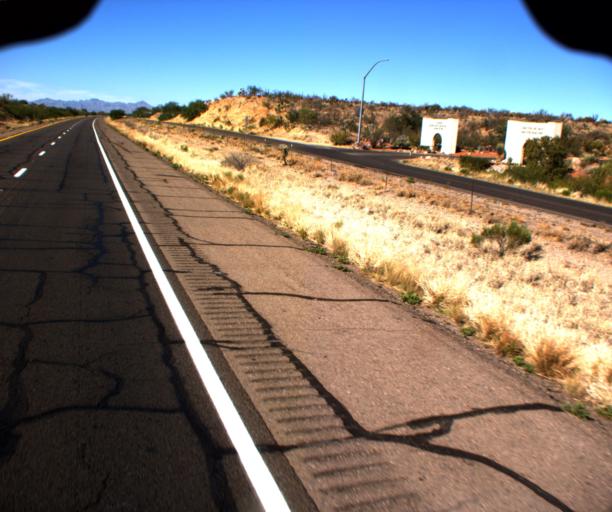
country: US
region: Arizona
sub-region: Pima County
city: Green Valley
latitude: 31.8276
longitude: -111.0027
